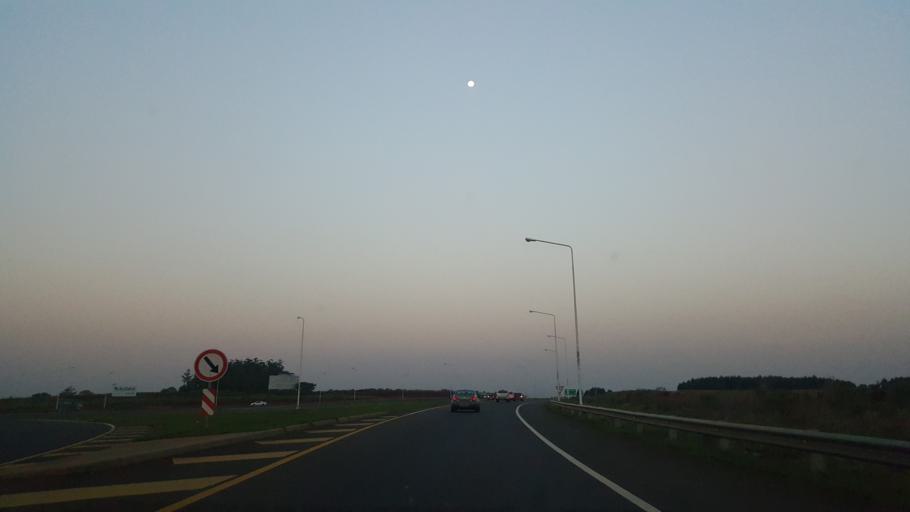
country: AR
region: Misiones
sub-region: Departamento de Capital
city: Posadas
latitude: -27.4477
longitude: -56.0348
